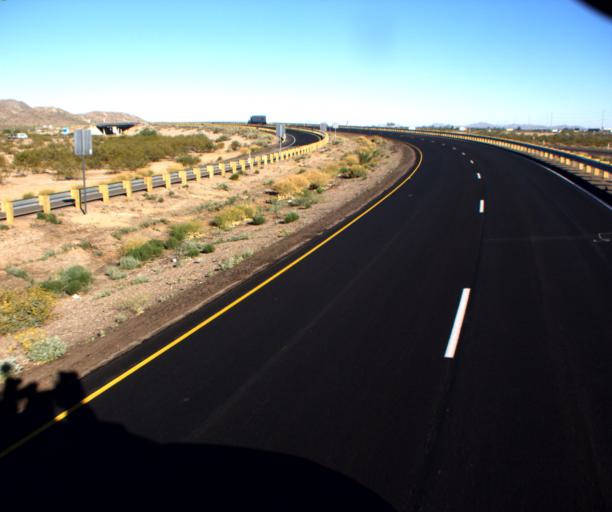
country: US
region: Arizona
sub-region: Pinal County
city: Arizona City
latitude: 32.8178
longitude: -111.6794
